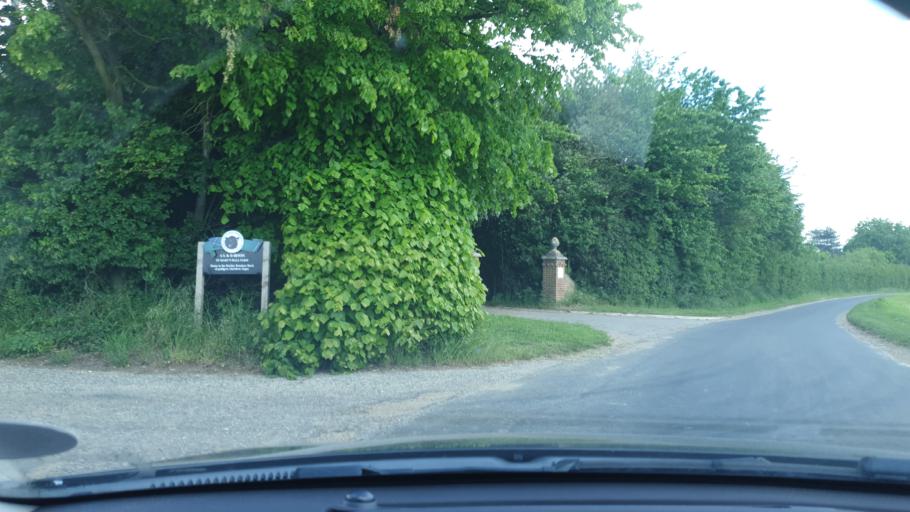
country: GB
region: England
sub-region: Essex
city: Great Bentley
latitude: 51.8482
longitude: 1.0762
